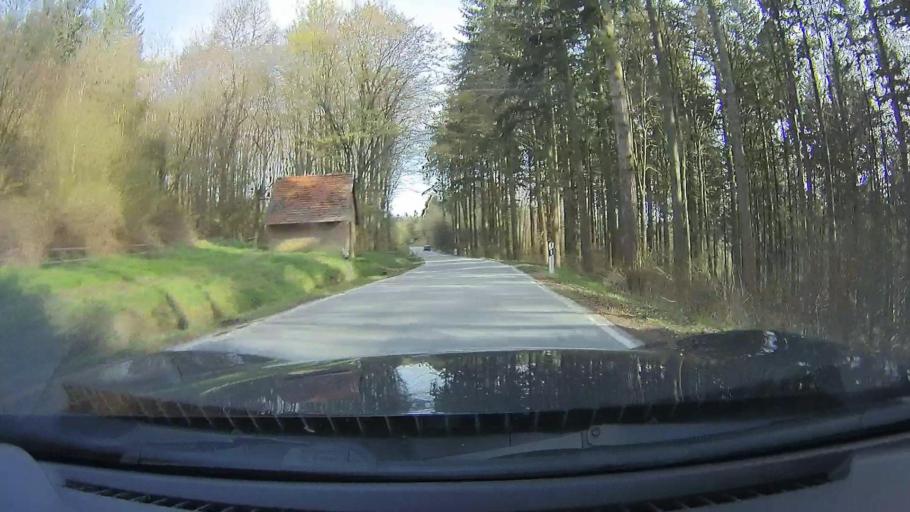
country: DE
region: Baden-Wuerttemberg
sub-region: Karlsruhe Region
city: Walldurn
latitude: 49.6152
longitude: 9.3318
